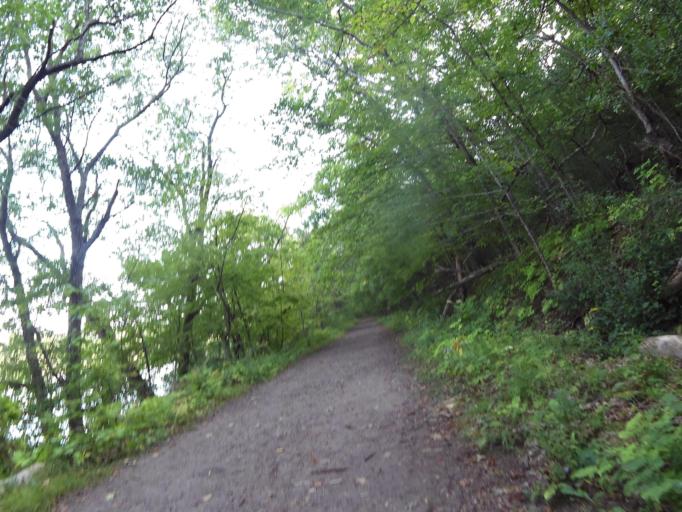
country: US
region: Minnesota
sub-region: Washington County
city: Afton
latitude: 44.8463
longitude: -92.7709
